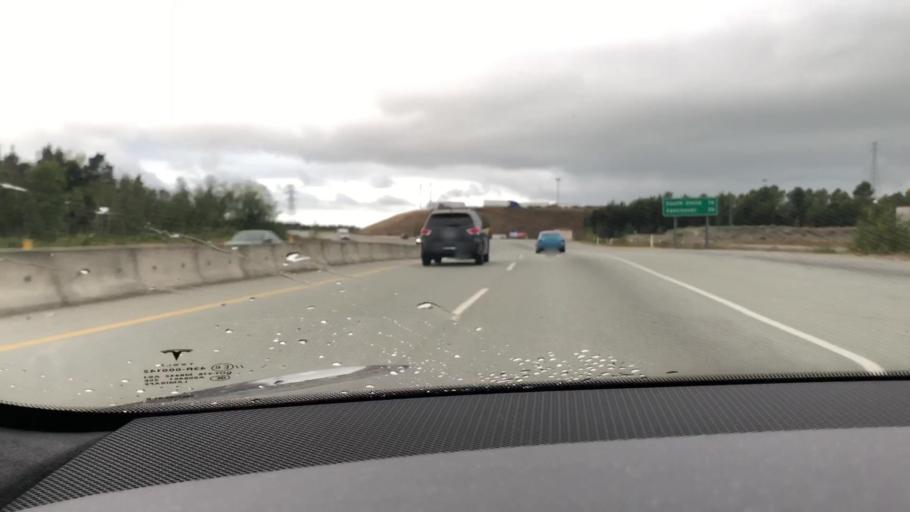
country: CA
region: British Columbia
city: Delta
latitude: 49.1480
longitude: -122.9656
